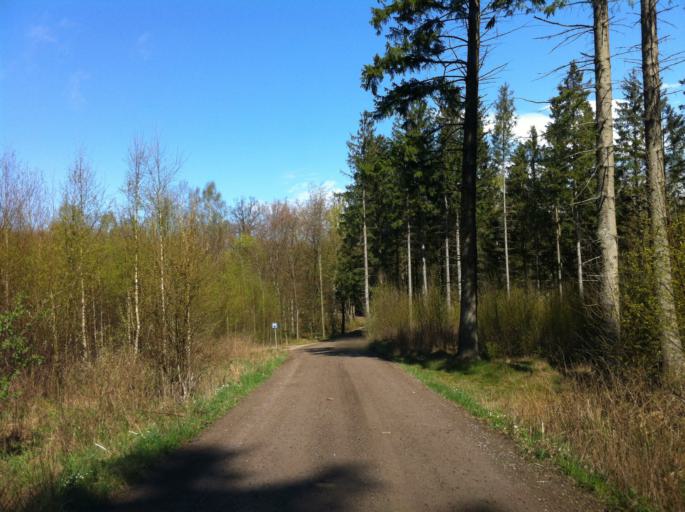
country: SE
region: Skane
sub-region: Horby Kommun
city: Hoerby
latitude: 55.8834
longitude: 13.6466
